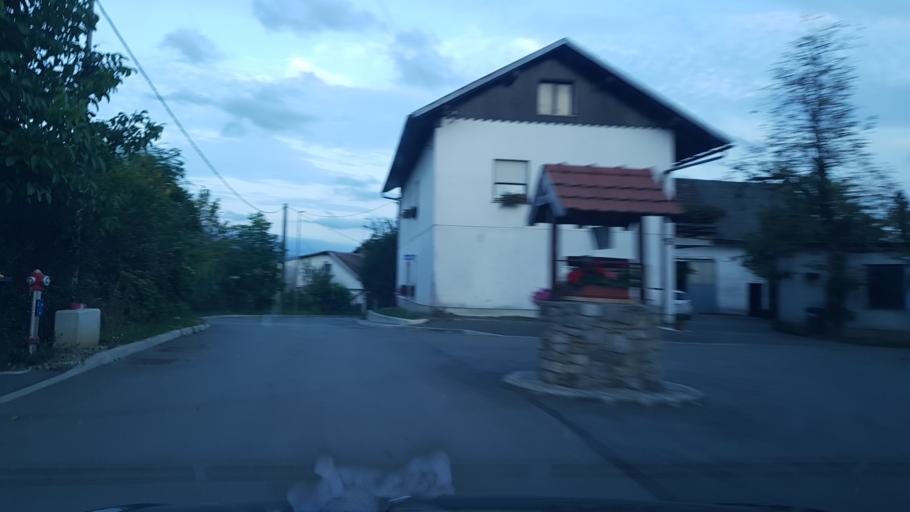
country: SI
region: Postojna
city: Postojna
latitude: 45.7501
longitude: 14.1790
